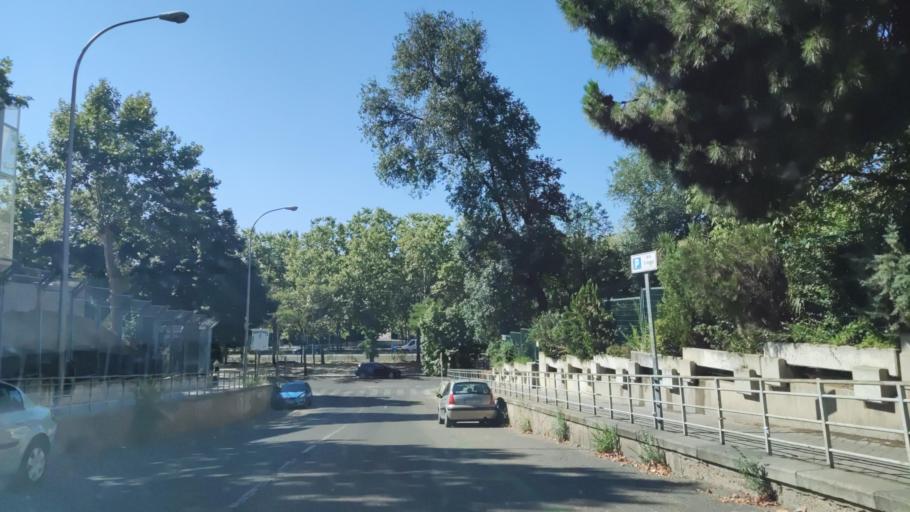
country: ES
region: Madrid
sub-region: Provincia de Madrid
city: Tetuan de las Victorias
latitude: 40.4822
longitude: -3.7086
